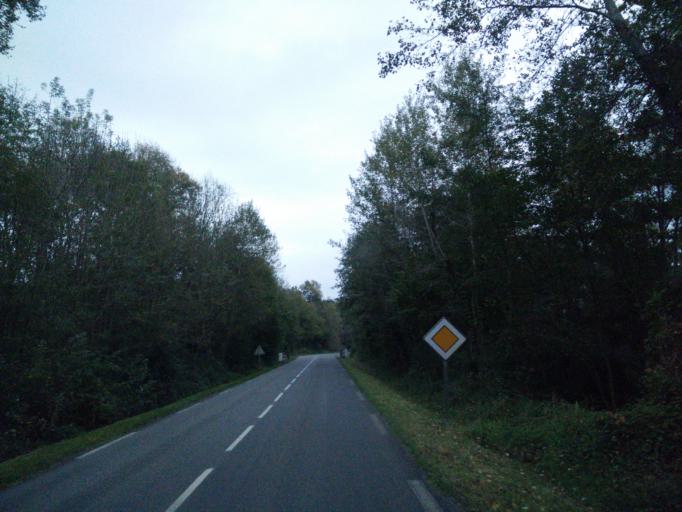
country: FR
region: Aquitaine
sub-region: Departement de la Dordogne
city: Carsac-Aillac
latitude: 44.7966
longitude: 1.3024
